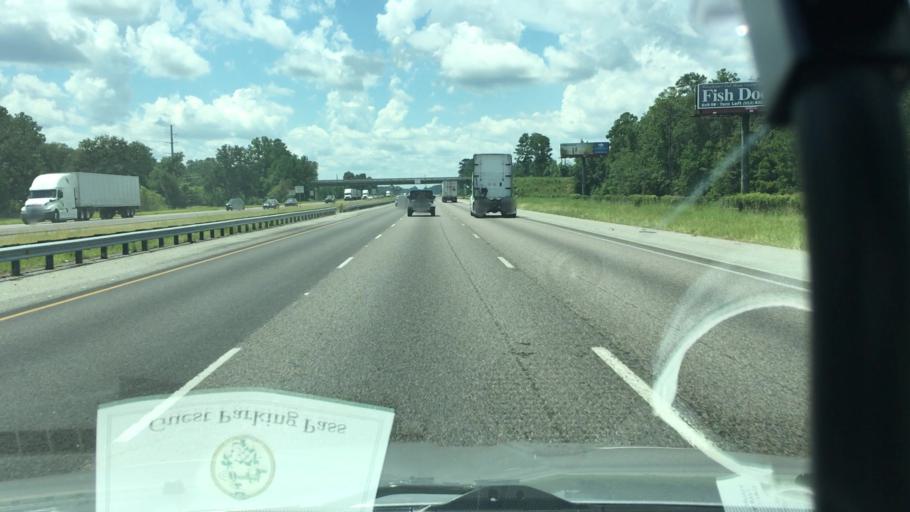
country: US
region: Georgia
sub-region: Liberty County
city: Midway
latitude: 31.8177
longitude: -81.3615
